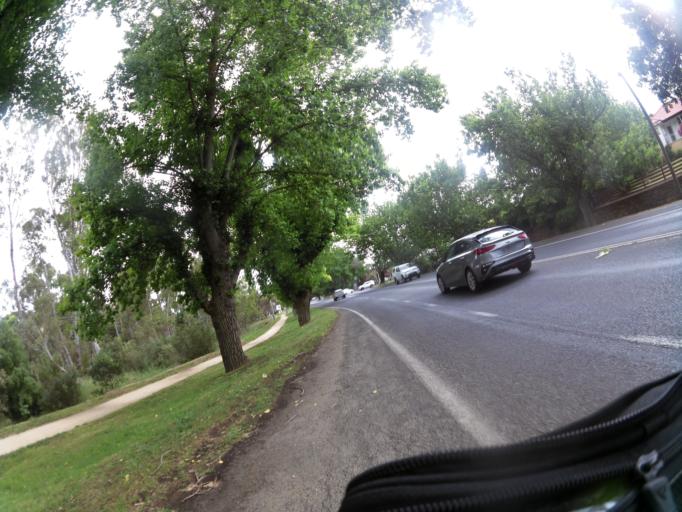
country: AU
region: Victoria
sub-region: Mount Alexander
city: Castlemaine
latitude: -37.0718
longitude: 144.2094
